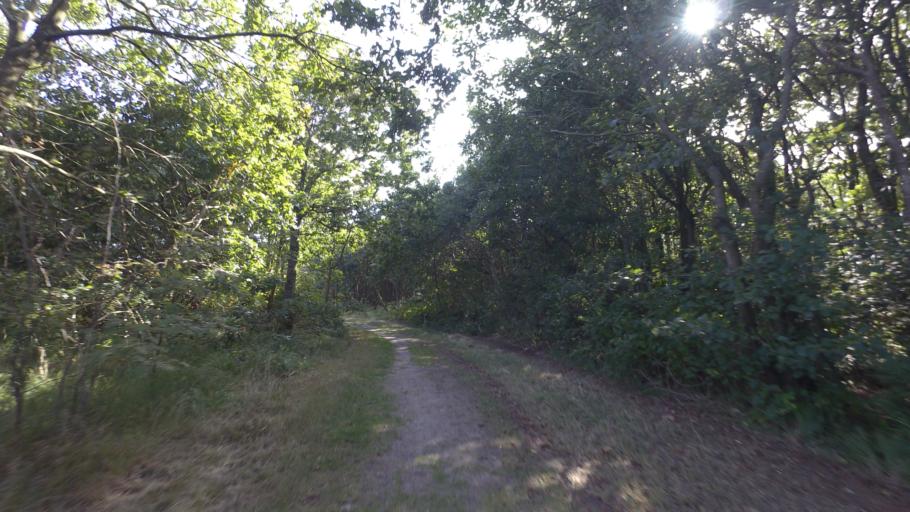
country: NL
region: Friesland
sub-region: Gemeente Ameland
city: Hollum
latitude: 53.4497
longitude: 5.7007
